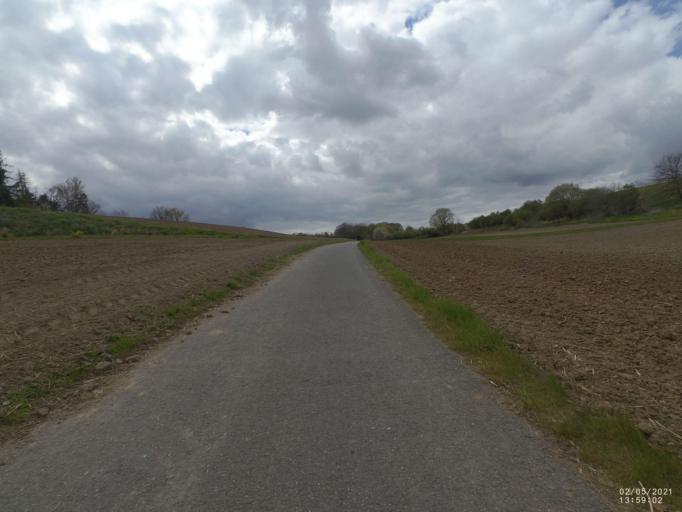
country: DE
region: Rheinland-Pfalz
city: Bassenheim
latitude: 50.3691
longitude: 7.4746
